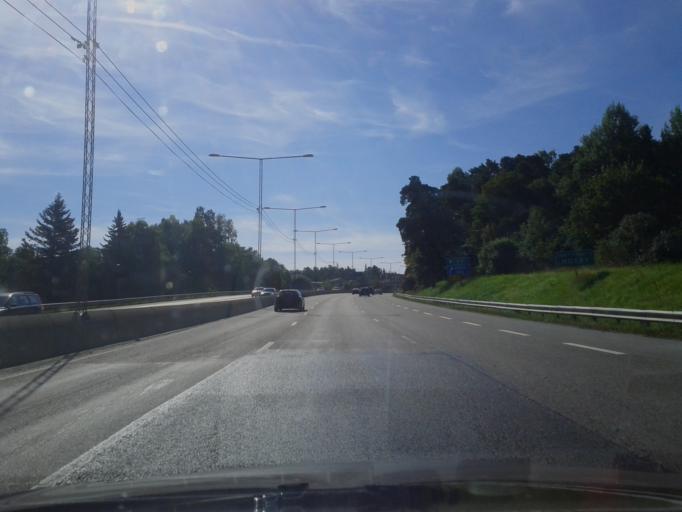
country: SE
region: Stockholm
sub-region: Danderyds Kommun
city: Djursholm
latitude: 59.4067
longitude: 18.0354
